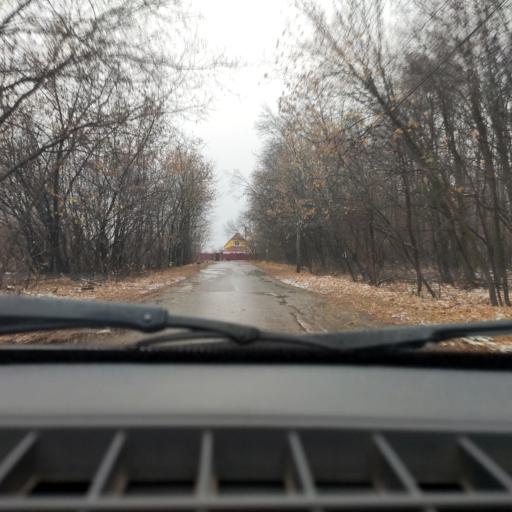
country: RU
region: Bashkortostan
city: Avdon
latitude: 54.6867
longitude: 55.7926
